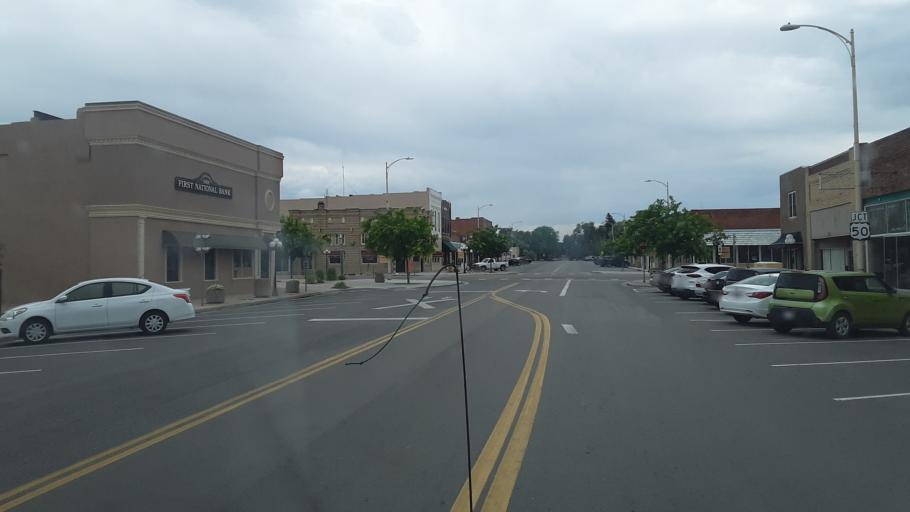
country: US
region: Colorado
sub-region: Otero County
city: Fowler
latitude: 38.1315
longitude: -104.0236
